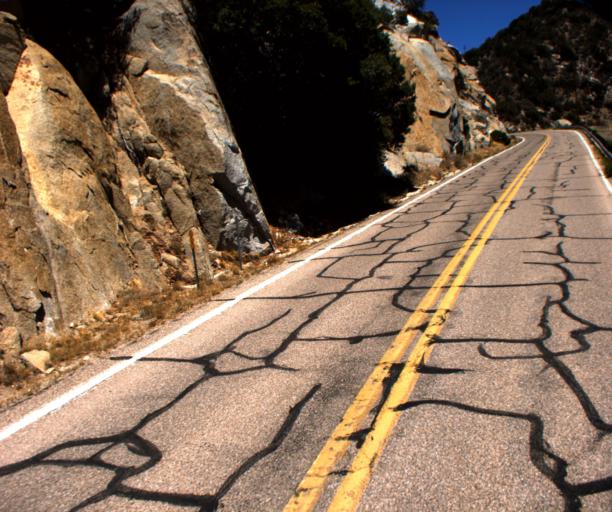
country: US
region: Arizona
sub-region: Pima County
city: Sells
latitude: 31.9568
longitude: -111.6081
